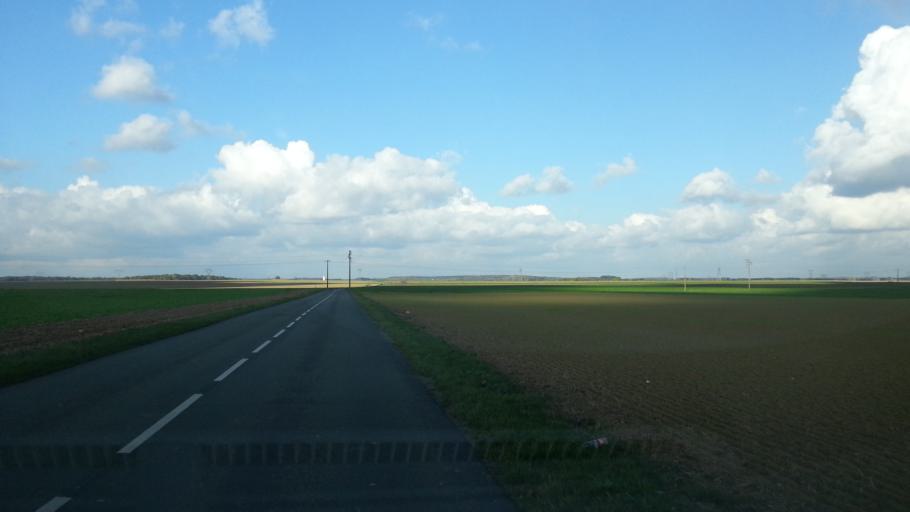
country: FR
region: Picardie
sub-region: Departement de l'Oise
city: Villers-sous-Saint-Leu
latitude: 49.2307
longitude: 2.4124
